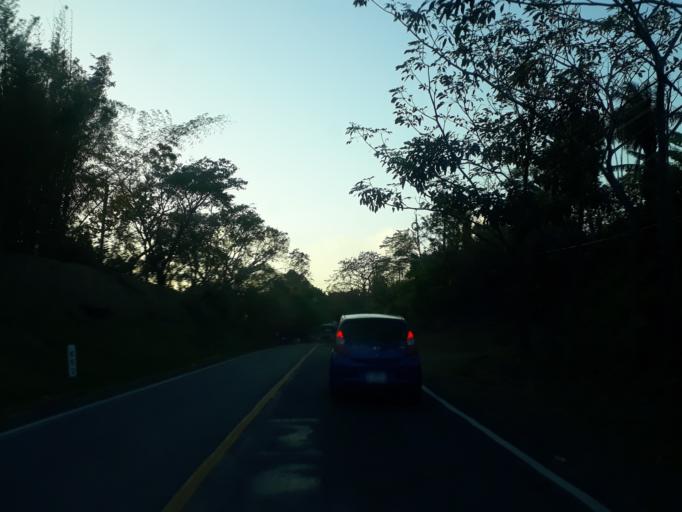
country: NI
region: Masaya
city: Niquinohomo
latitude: 11.9008
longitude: -86.1175
